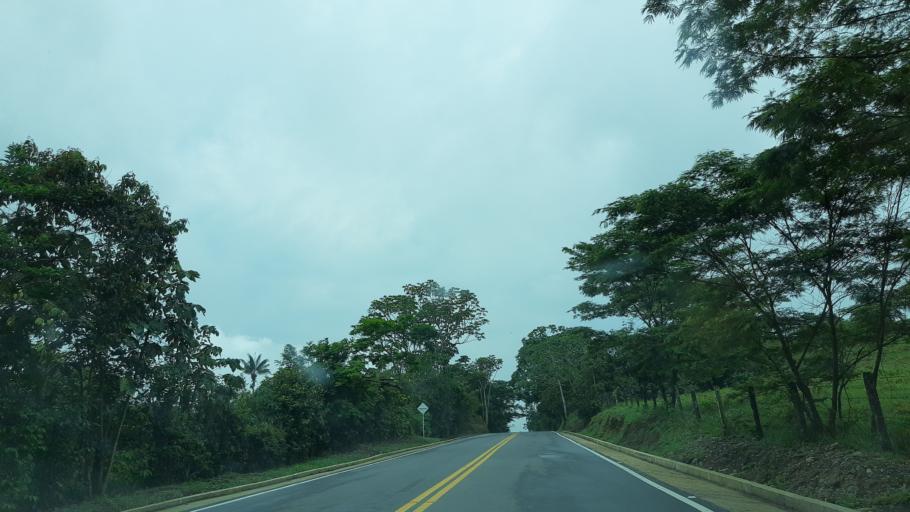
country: CO
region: Casanare
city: Sabanalarga
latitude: 4.7709
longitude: -73.0411
